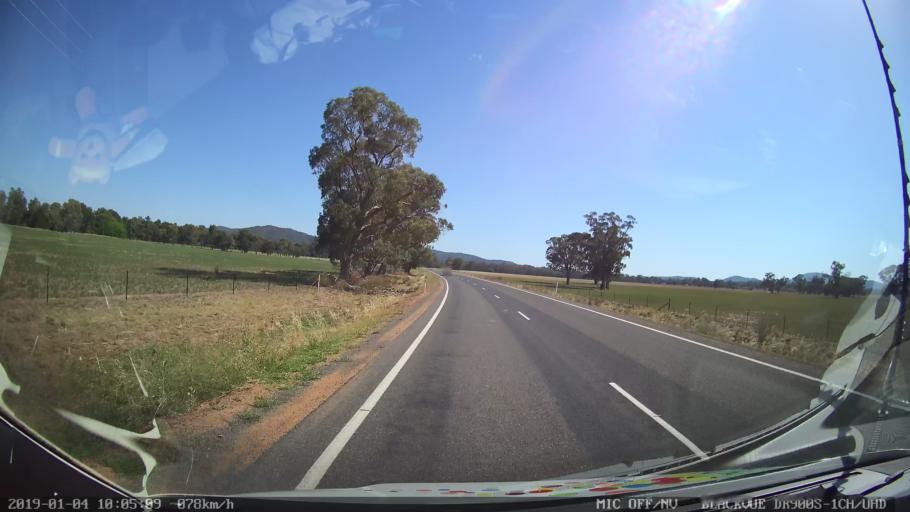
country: AU
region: New South Wales
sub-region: Cabonne
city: Canowindra
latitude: -33.4450
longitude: 148.3642
